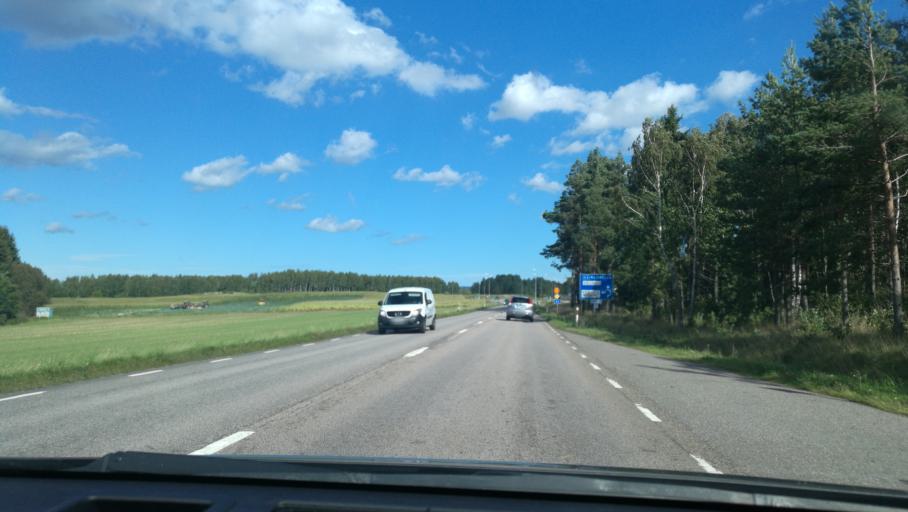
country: SE
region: Vaestra Goetaland
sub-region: Gotene Kommun
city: Kallby
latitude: 58.4974
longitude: 13.2998
